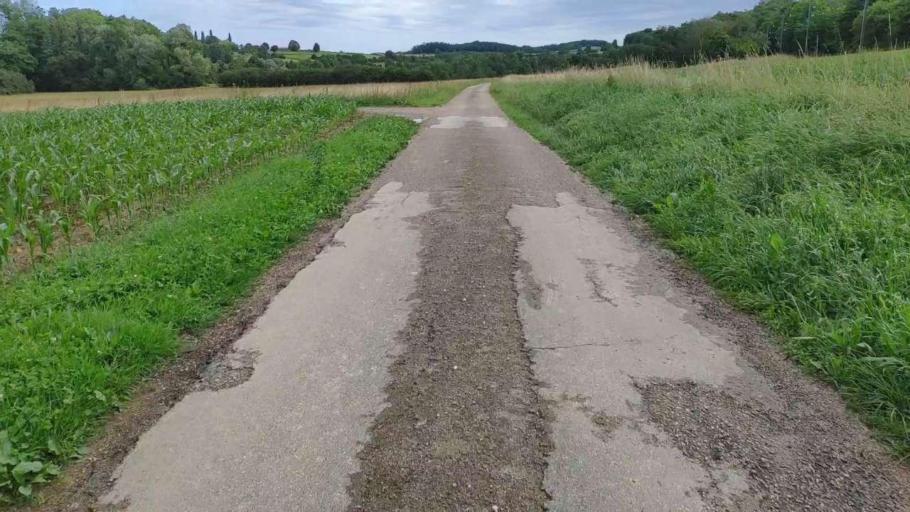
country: FR
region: Franche-Comte
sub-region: Departement du Jura
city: Poligny
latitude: 46.8082
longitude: 5.6070
